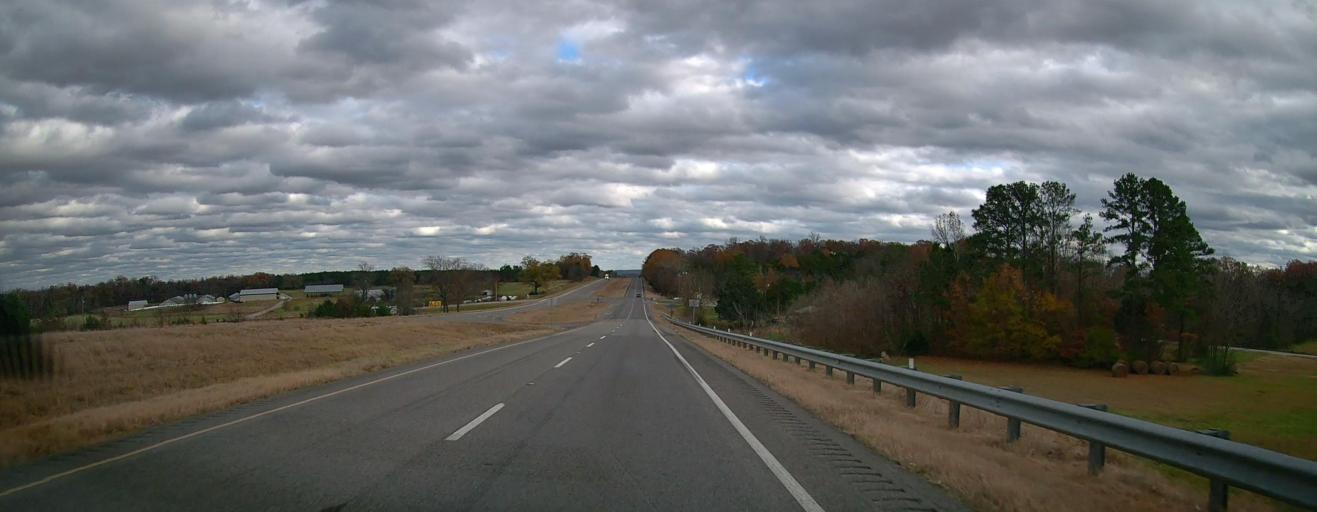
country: US
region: Alabama
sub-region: Morgan County
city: Danville
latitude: 34.3950
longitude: -87.1220
